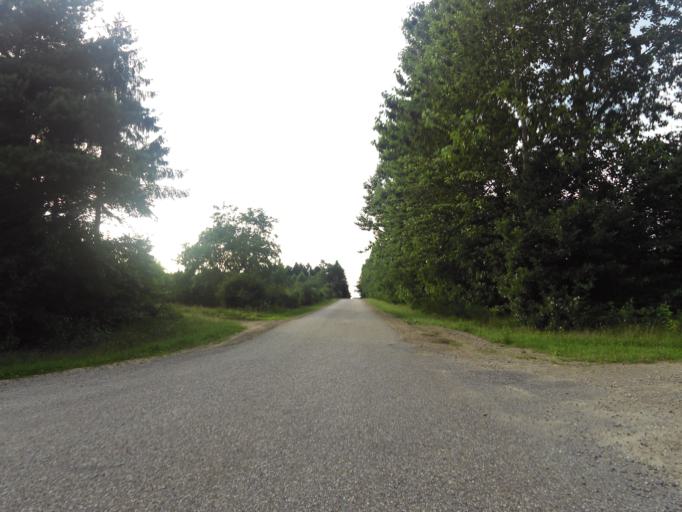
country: DK
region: South Denmark
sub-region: Tonder Kommune
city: Logumkloster
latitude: 55.1591
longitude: 8.9307
